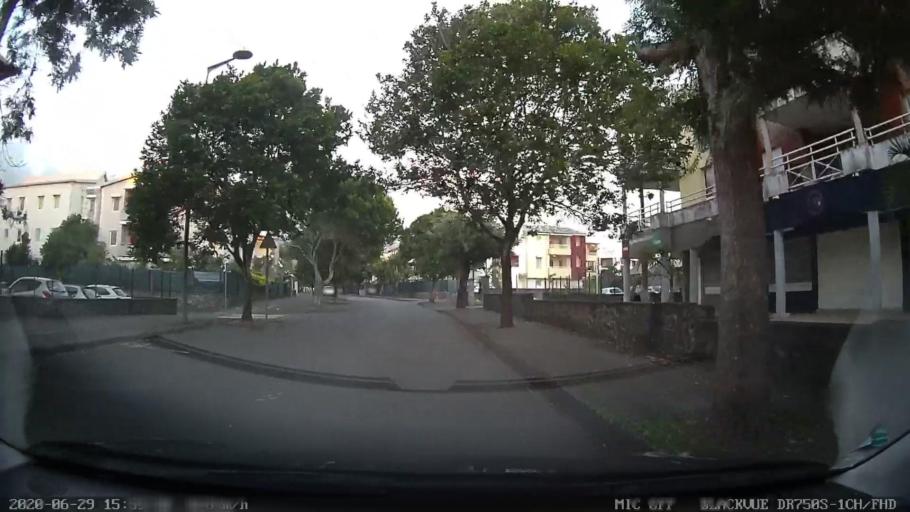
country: RE
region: Reunion
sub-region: Reunion
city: Bras-Panon
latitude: -21.0011
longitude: 55.6909
